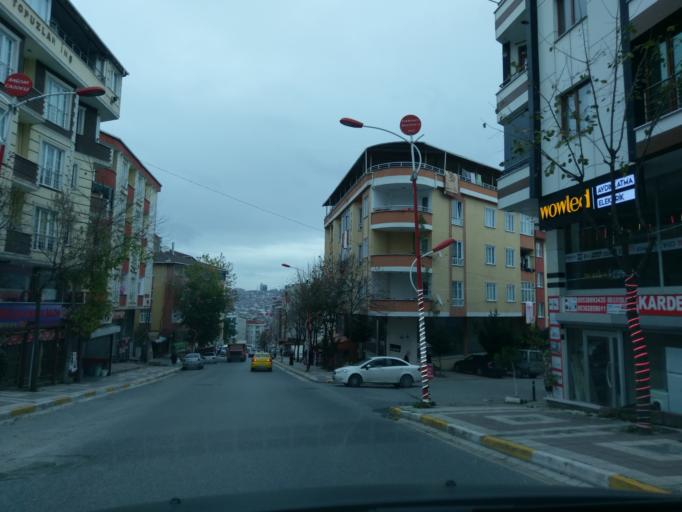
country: TR
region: Istanbul
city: Esenyurt
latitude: 41.0166
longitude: 28.6638
